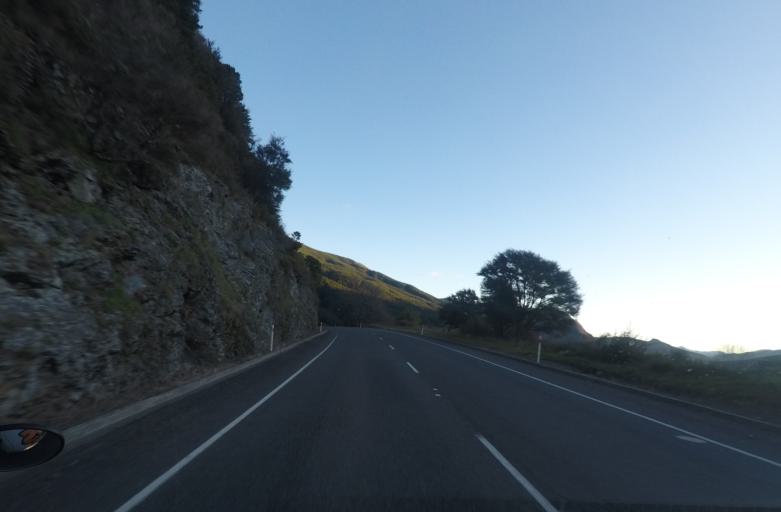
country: NZ
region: Marlborough
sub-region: Marlborough District
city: Picton
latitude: -41.2776
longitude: 173.7292
